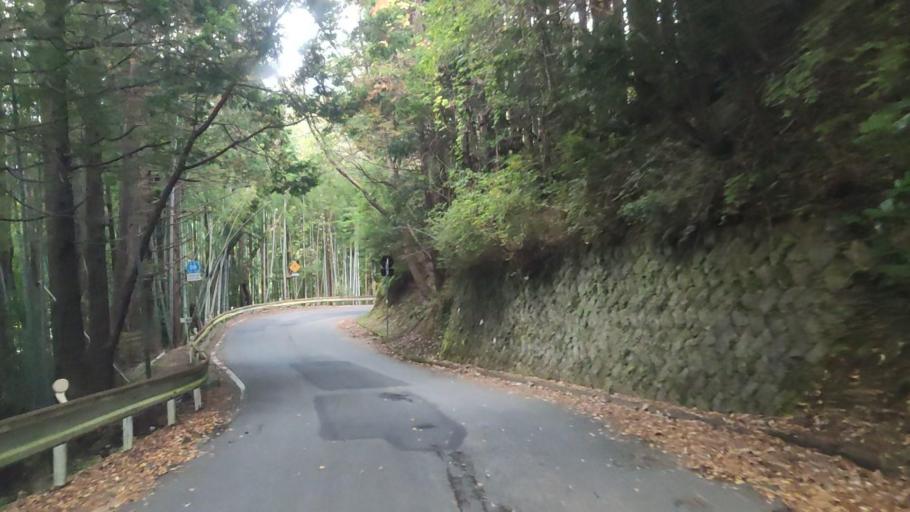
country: JP
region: Shizuoka
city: Ito
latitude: 34.9546
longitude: 139.0515
